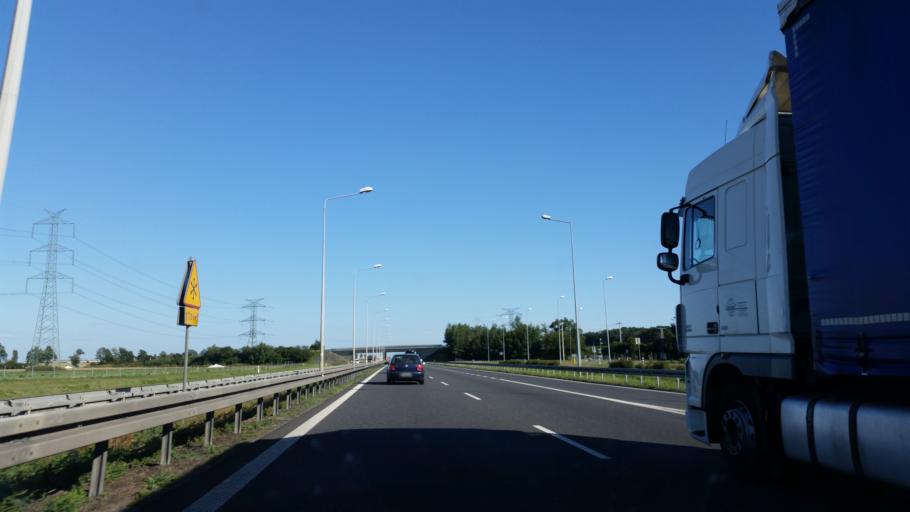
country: PL
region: Opole Voivodeship
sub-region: Powiat brzeski
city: Grodkow
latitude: 50.7653
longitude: 17.4126
